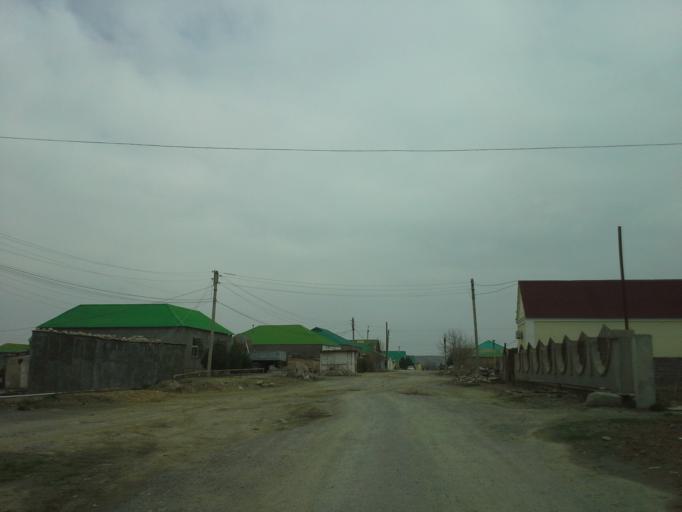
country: TM
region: Ahal
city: Abadan
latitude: 37.9740
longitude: 58.2266
